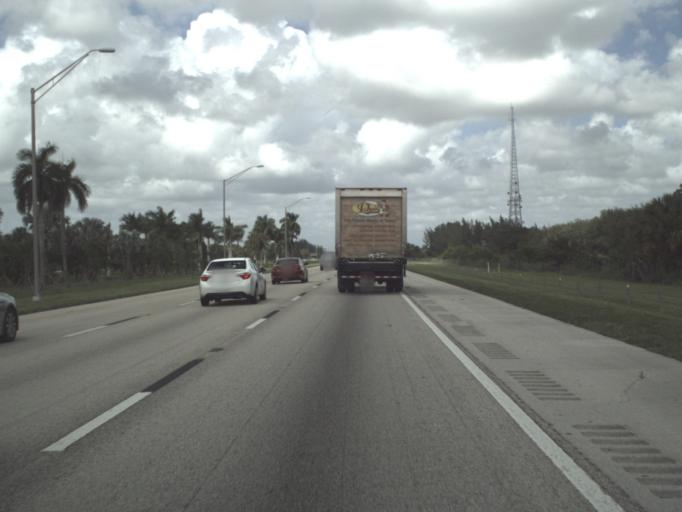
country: US
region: Florida
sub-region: Palm Beach County
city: Greenacres City
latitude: 26.6390
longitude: -80.1739
